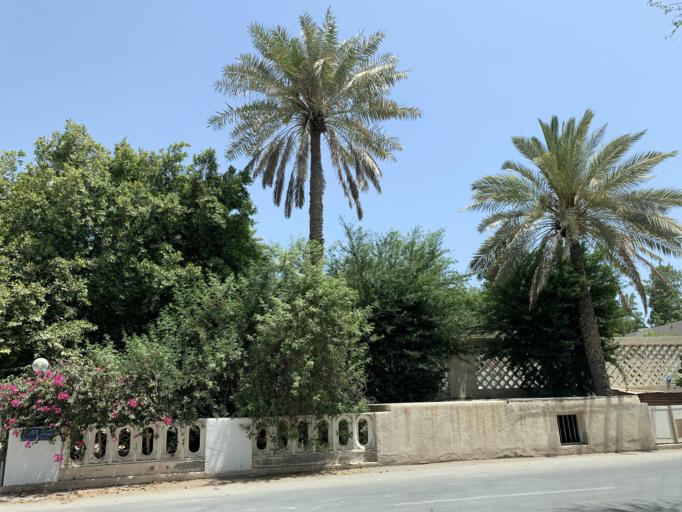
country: BH
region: Manama
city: Jidd Hafs
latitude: 26.2233
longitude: 50.4792
